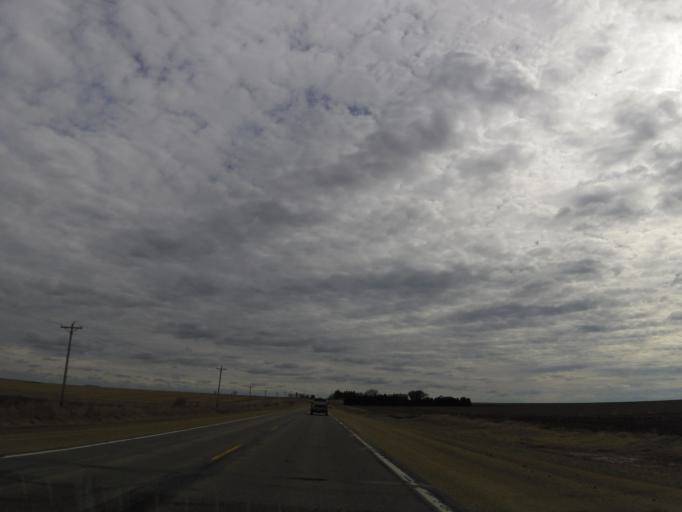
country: US
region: Iowa
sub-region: Howard County
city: Cresco
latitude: 43.3070
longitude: -92.2990
